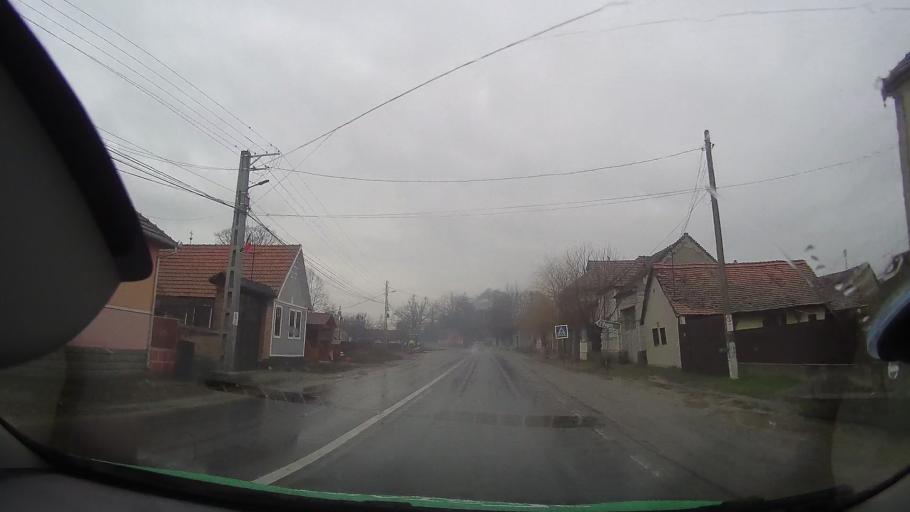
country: RO
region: Bihor
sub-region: Comuna Sambata
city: Sambata
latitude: 46.8006
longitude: 22.2026
